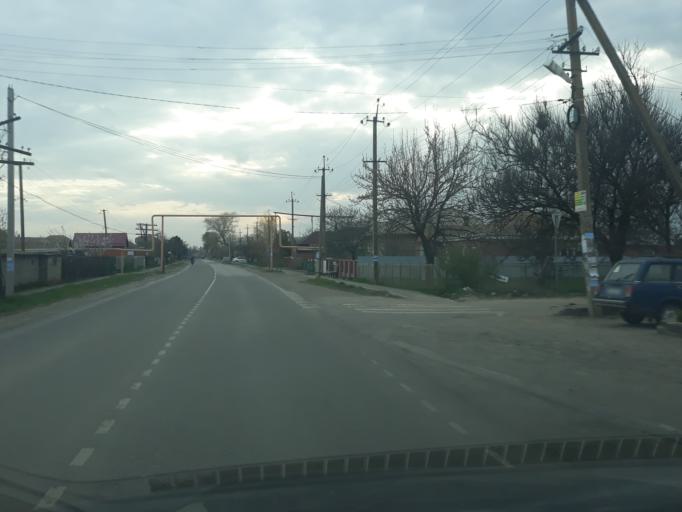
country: RU
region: Rostov
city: Novobessergenovka
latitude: 47.1745
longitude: 38.7634
